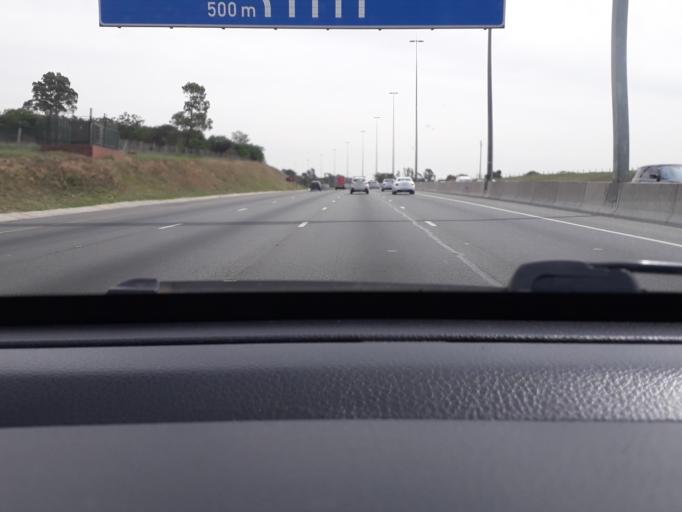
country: ZA
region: Gauteng
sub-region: City of Johannesburg Metropolitan Municipality
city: Diepsloot
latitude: -26.0640
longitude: 27.9806
